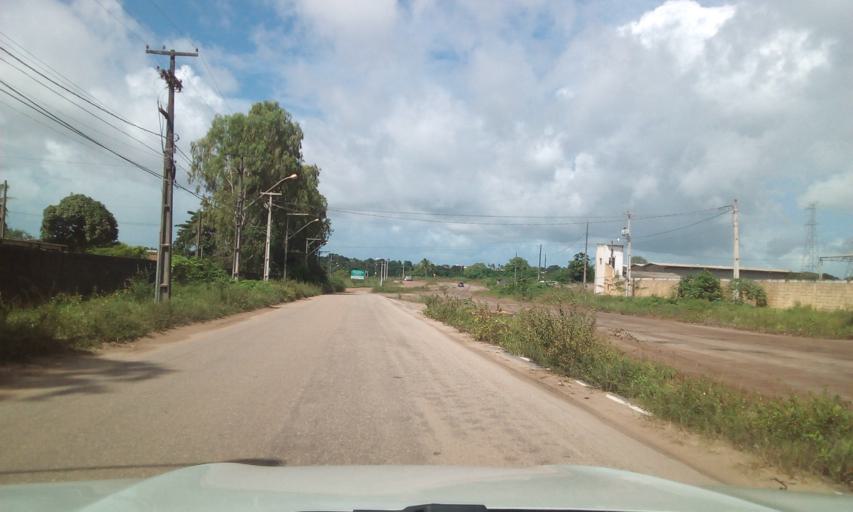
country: BR
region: Paraiba
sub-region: Conde
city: Conde
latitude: -7.1934
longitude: -34.9005
